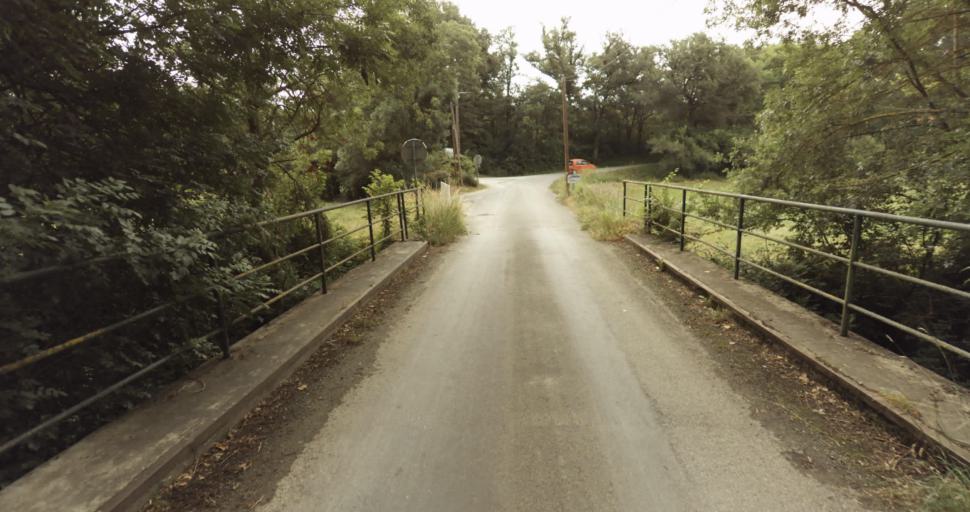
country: FR
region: Midi-Pyrenees
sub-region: Departement de la Haute-Garonne
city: Fontenilles
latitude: 43.5562
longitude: 1.2117
